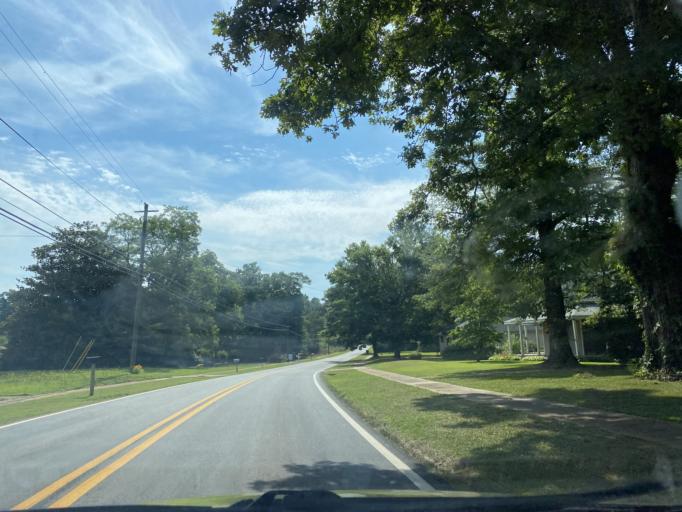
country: US
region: Georgia
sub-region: Coweta County
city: Grantville
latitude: 33.2103
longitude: -84.7412
